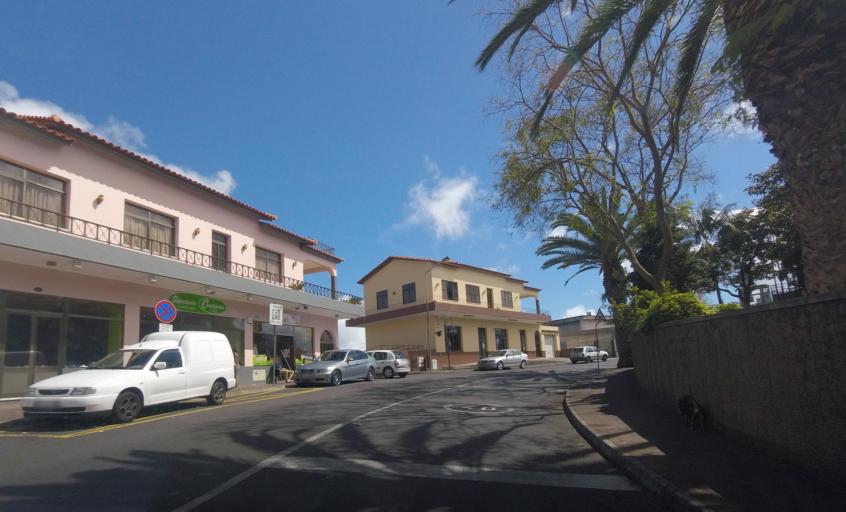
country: PT
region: Madeira
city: Camara de Lobos
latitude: 32.6729
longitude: -16.9780
